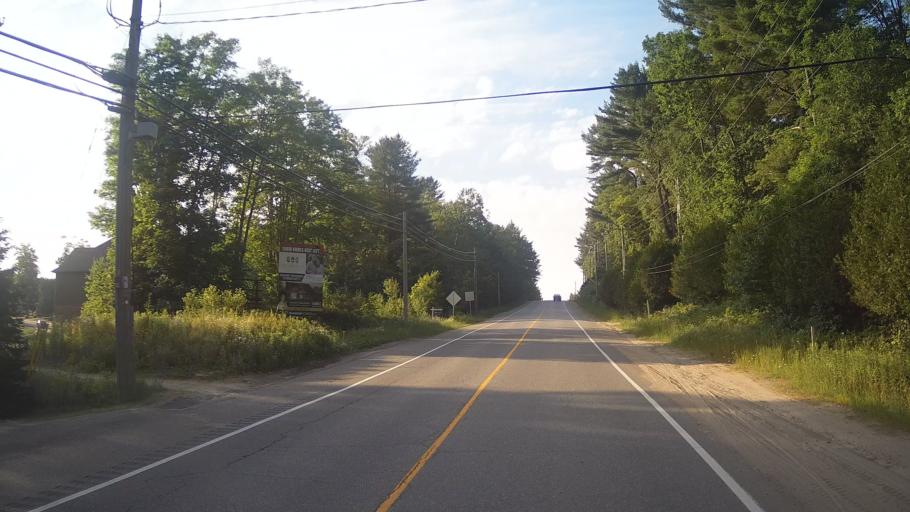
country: CA
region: Ontario
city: Huntsville
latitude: 45.3542
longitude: -79.2024
